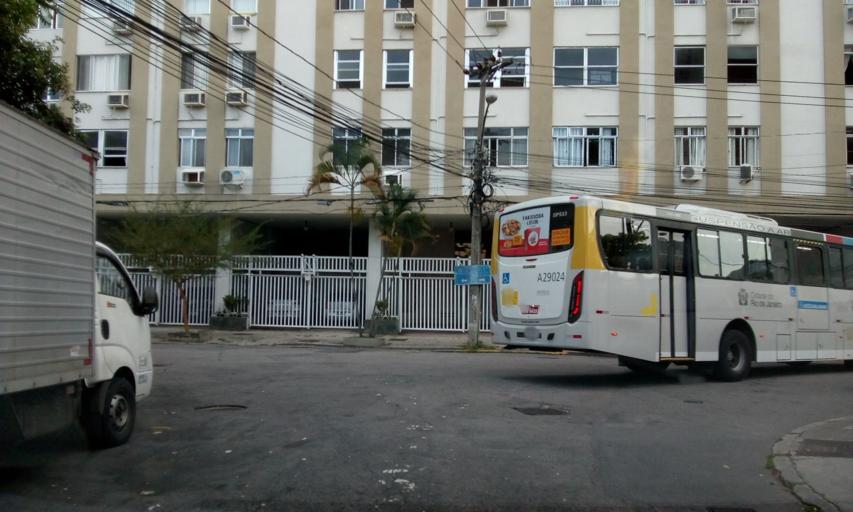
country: BR
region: Rio de Janeiro
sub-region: Rio De Janeiro
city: Rio de Janeiro
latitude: -22.9545
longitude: -43.1737
